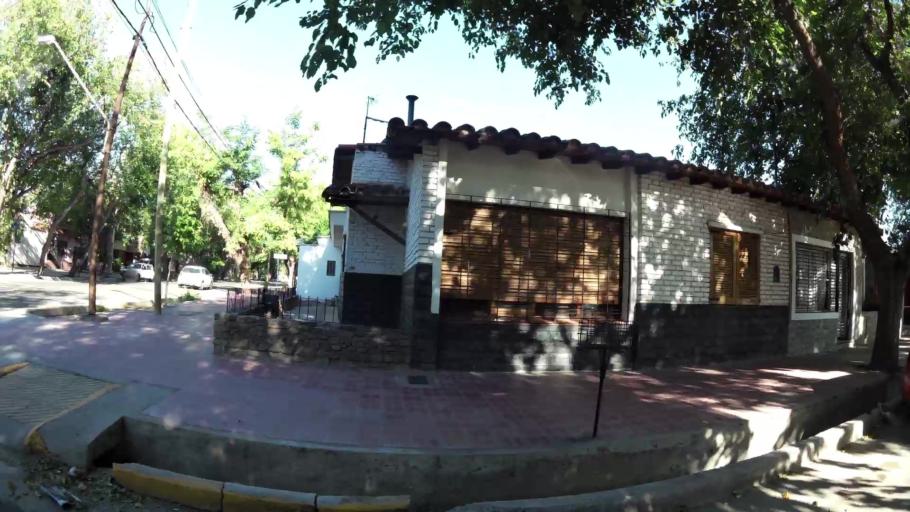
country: AR
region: Mendoza
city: Las Heras
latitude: -32.8644
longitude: -68.8476
